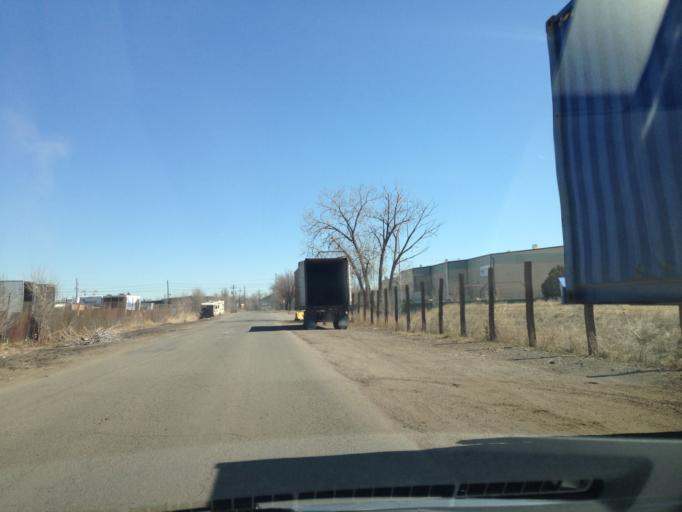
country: US
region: Colorado
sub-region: Adams County
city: Commerce City
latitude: 39.7954
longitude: -104.9722
